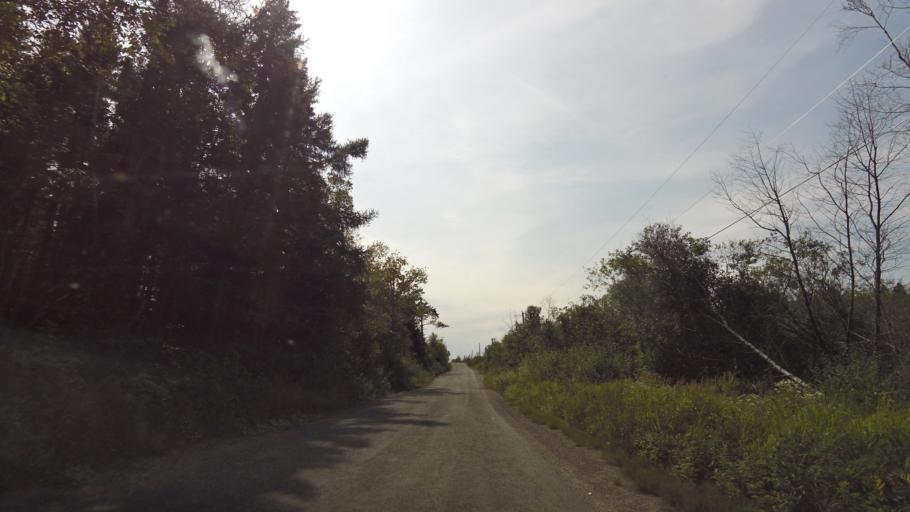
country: CA
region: New Brunswick
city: Hampton
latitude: 45.5672
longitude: -65.8379
